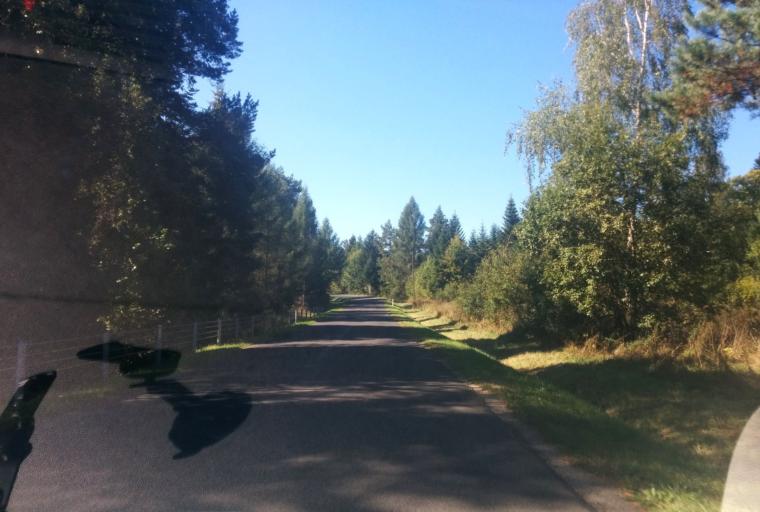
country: PL
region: Subcarpathian Voivodeship
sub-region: Powiat bieszczadzki
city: Czarna
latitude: 49.3177
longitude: 22.6536
